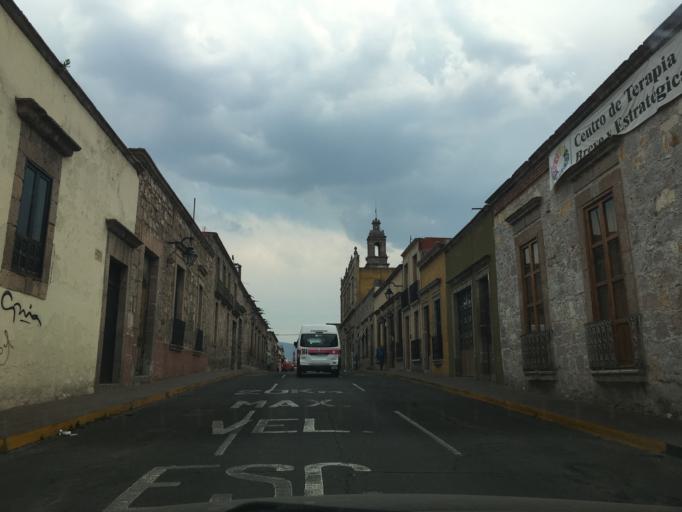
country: MX
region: Michoacan
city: Morelia
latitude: 19.7039
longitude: -101.1969
